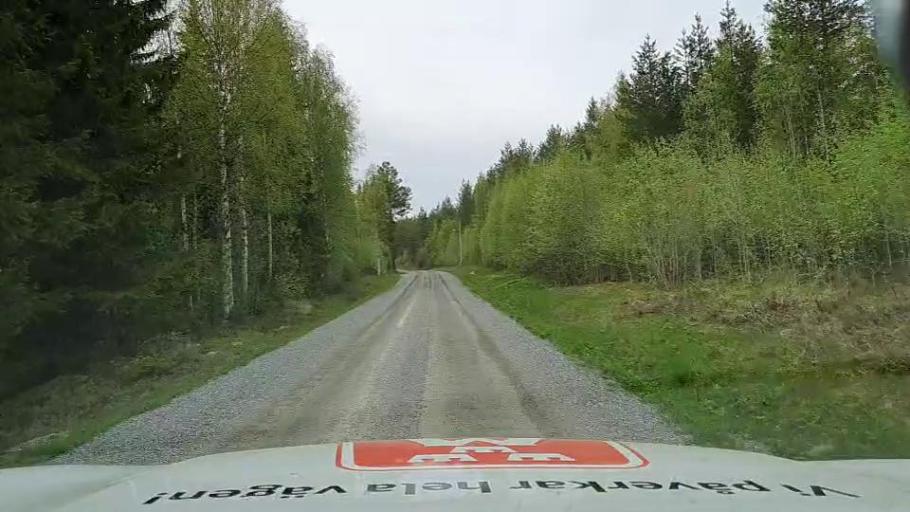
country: SE
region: Jaemtland
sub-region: Braecke Kommun
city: Braecke
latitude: 62.4647
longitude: 14.9189
